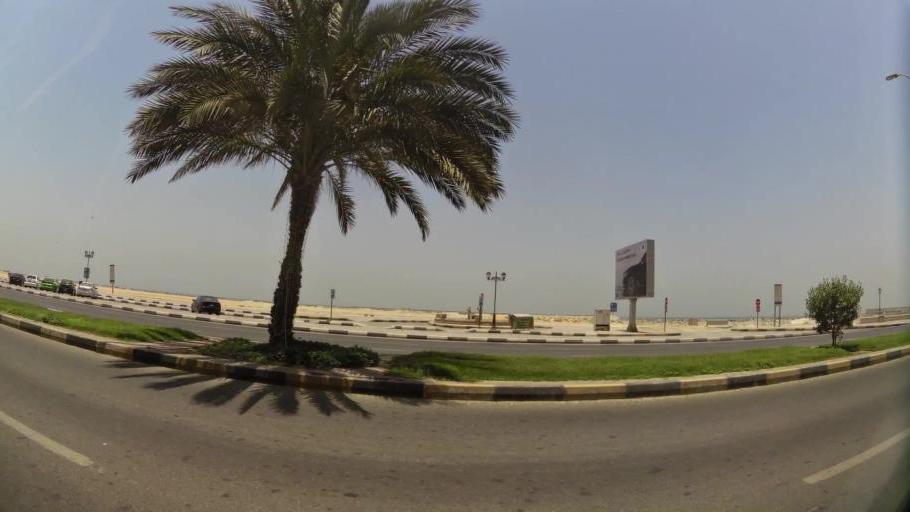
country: AE
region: Ajman
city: Ajman
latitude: 25.4140
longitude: 55.4370
